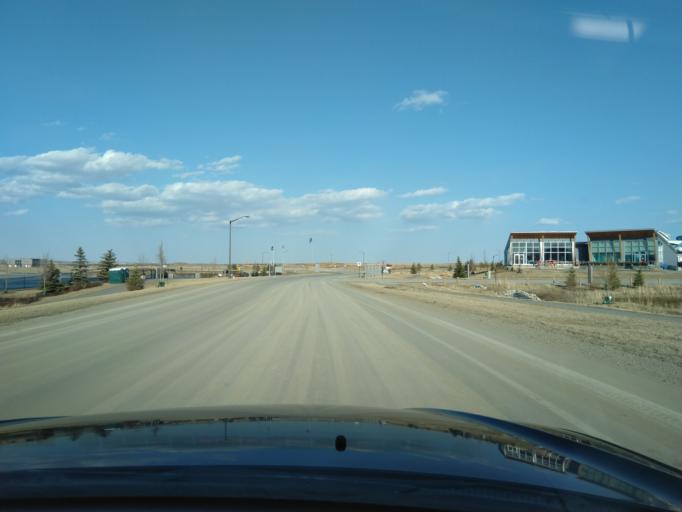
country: CA
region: Alberta
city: Cochrane
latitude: 51.1135
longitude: -114.3976
